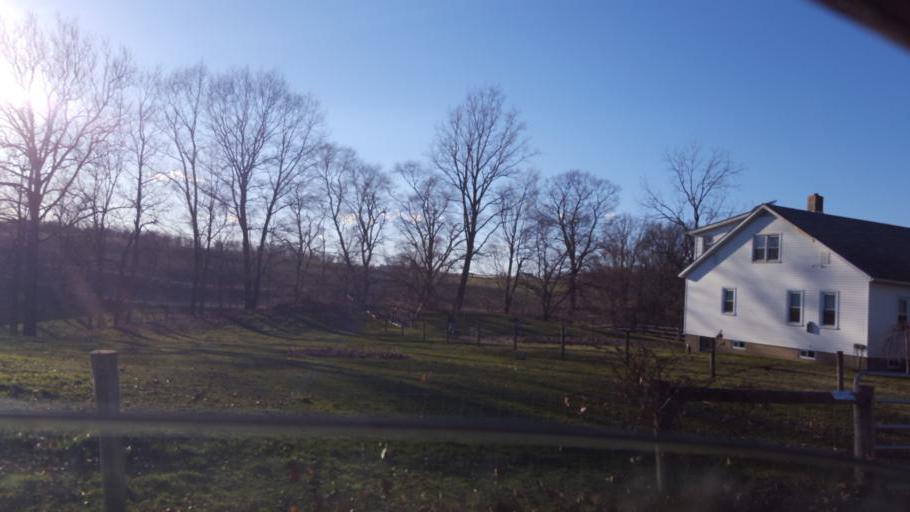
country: US
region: Ohio
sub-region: Wayne County
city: Apple Creek
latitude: 40.6367
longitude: -81.7650
